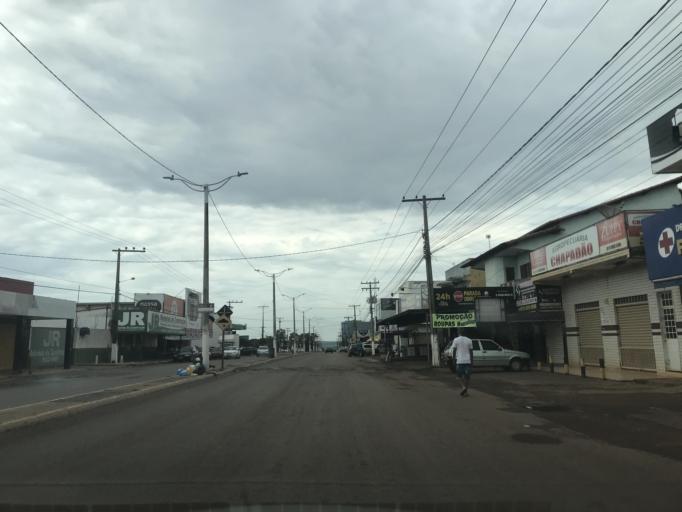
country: BR
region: Goias
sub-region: Luziania
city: Luziania
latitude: -16.2369
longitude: -47.9421
